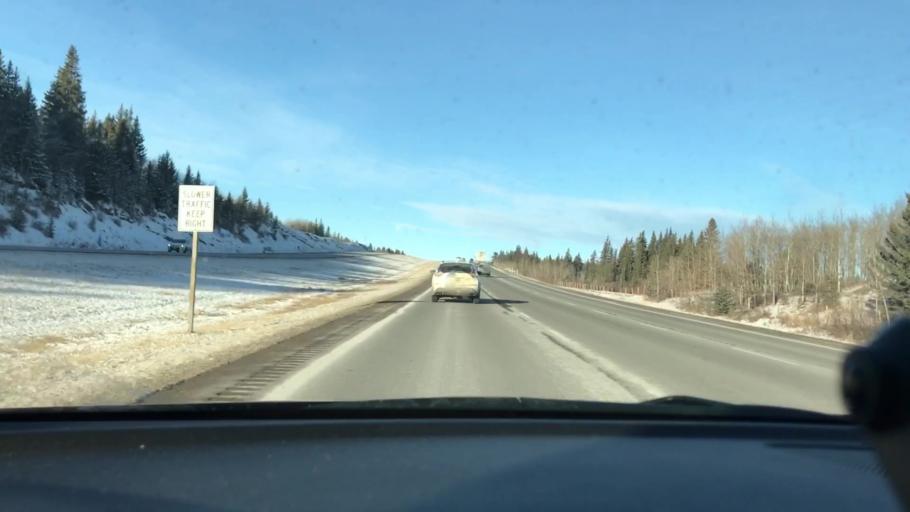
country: CA
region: Alberta
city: Cochrane
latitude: 51.1369
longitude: -114.7085
